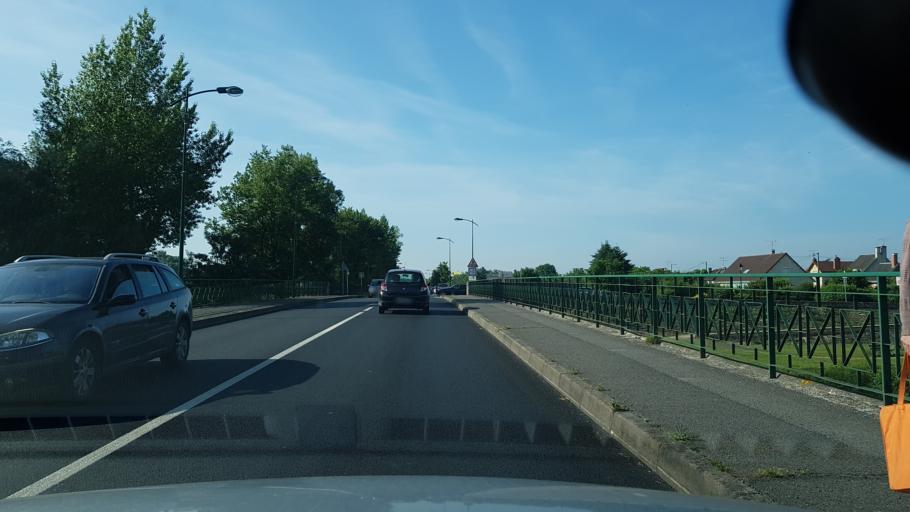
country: FR
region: Centre
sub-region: Departement du Loir-et-Cher
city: Selles-sur-Cher
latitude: 47.2784
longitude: 1.5579
